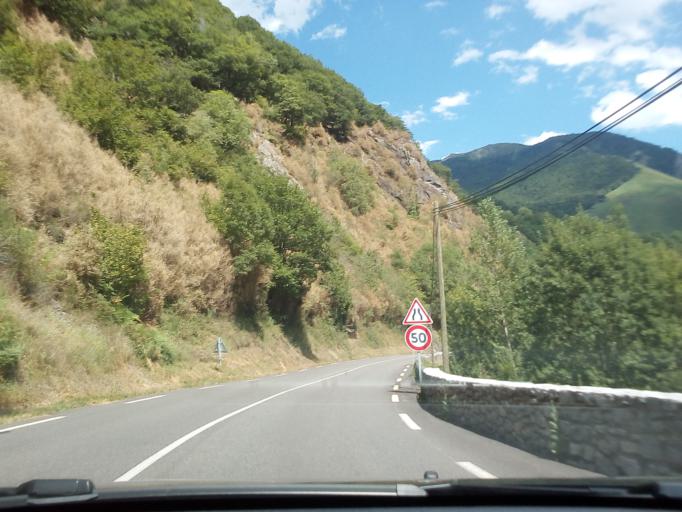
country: FR
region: Aquitaine
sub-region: Departement des Pyrenees-Atlantiques
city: Laruns
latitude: 42.9391
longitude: -0.5975
